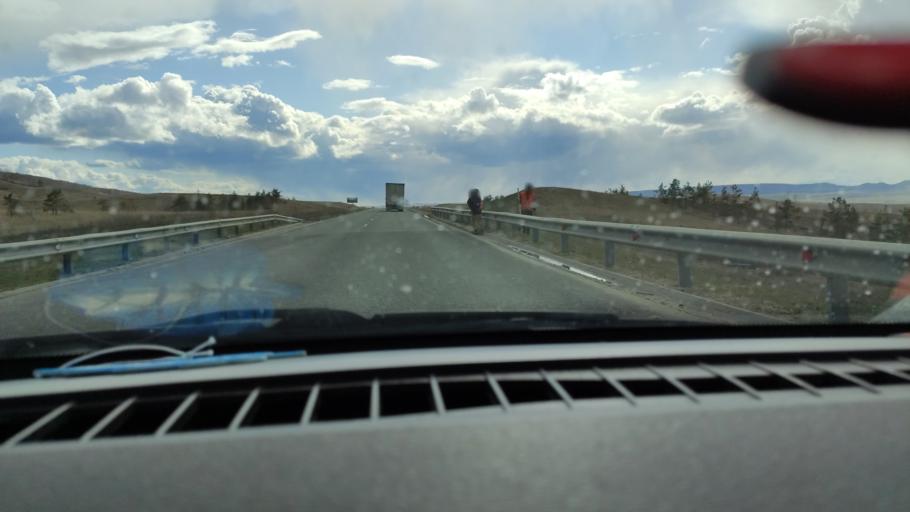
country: RU
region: Saratov
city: Alekseyevka
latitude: 52.3587
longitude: 47.9503
